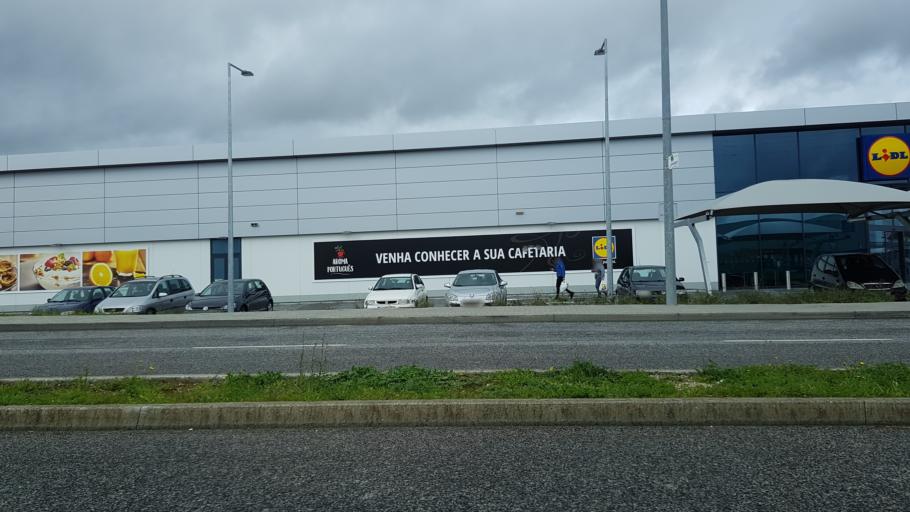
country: PT
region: Lisbon
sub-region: Alenquer
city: Carregado
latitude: 39.0401
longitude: -8.9882
